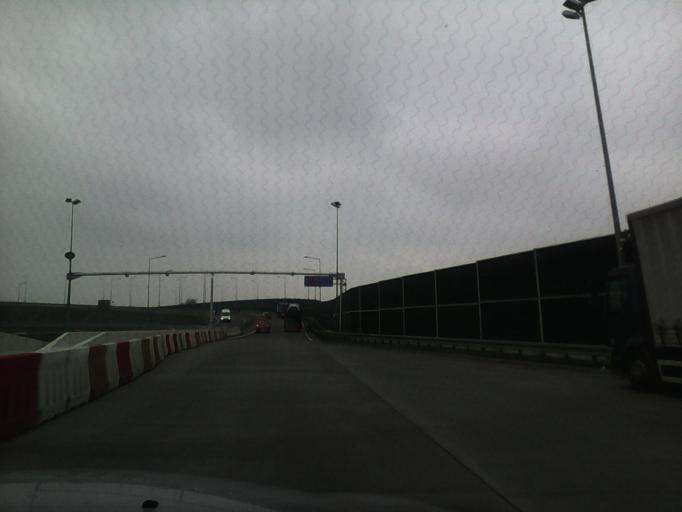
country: PL
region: Masovian Voivodeship
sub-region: Powiat zyrardowski
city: Wiskitki
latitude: 52.0892
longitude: 20.3589
